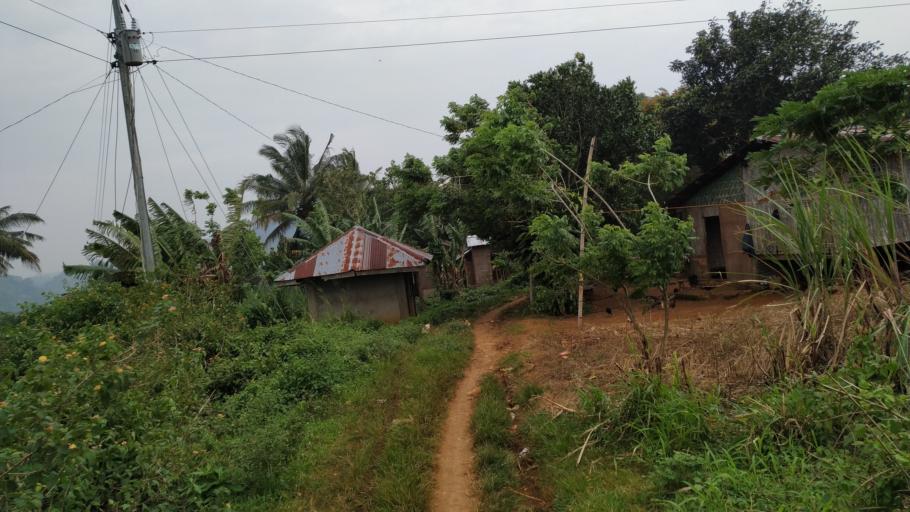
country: PH
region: Western Visayas
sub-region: Province of Negros Occidental
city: Quezon
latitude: 10.4211
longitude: 123.2411
